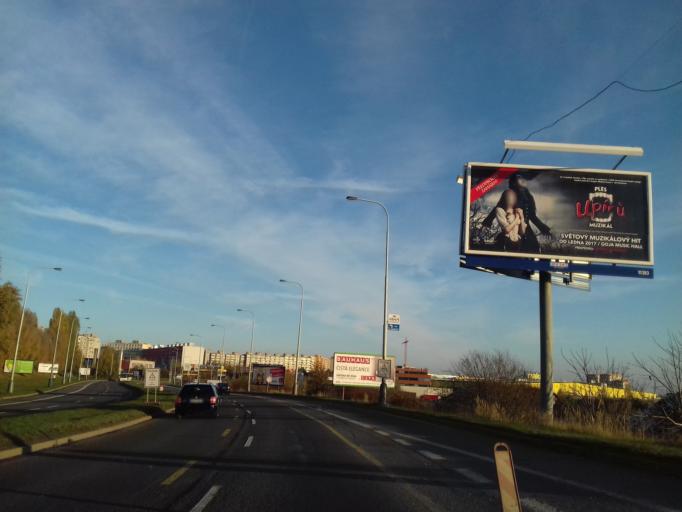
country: CZ
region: Central Bohemia
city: Hostivice
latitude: 50.0441
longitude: 14.3101
